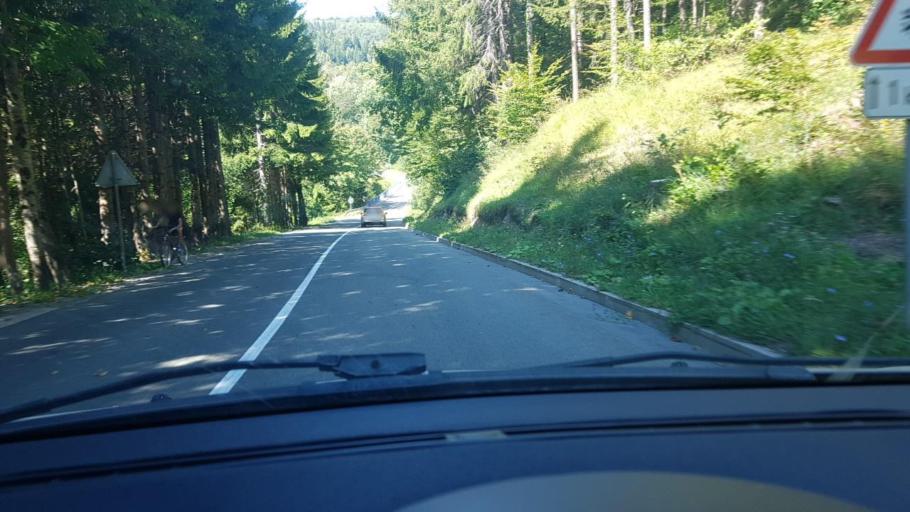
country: HR
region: Primorsko-Goranska
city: Vrbovsko
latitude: 45.3785
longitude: 14.9823
